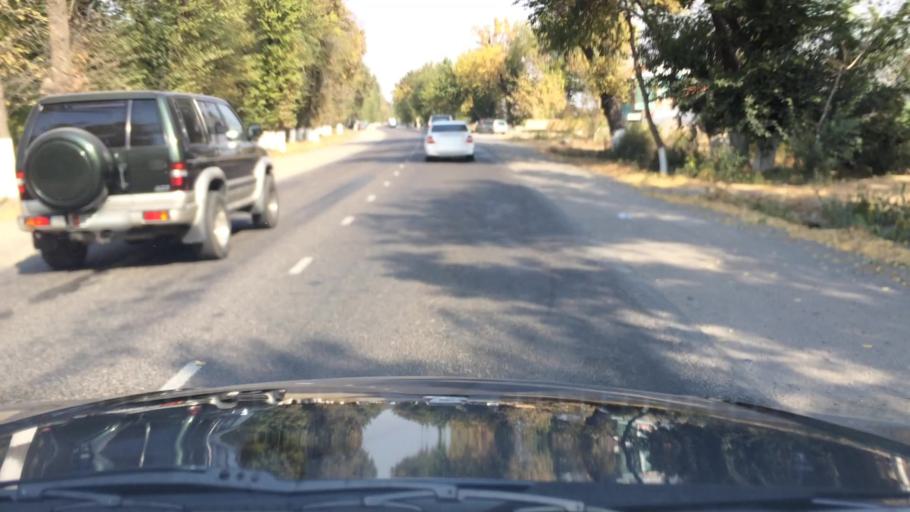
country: KG
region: Chuy
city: Lebedinovka
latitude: 42.9127
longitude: 74.6882
